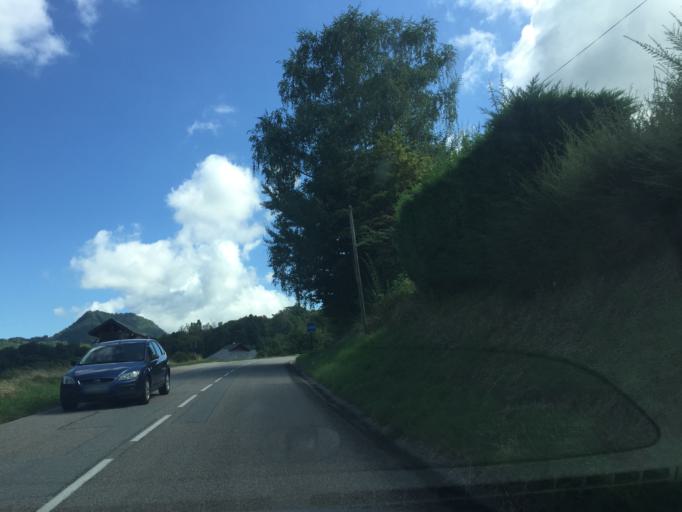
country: FR
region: Rhone-Alpes
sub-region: Departement de la Savoie
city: La Rochette
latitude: 45.4503
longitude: 6.1296
